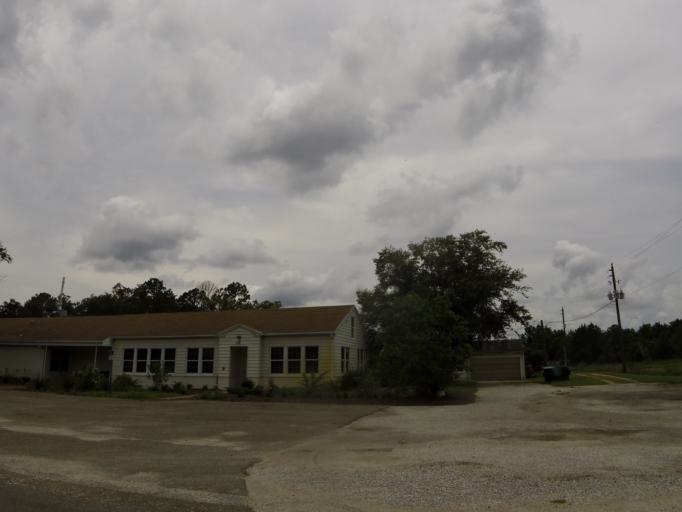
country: US
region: Florida
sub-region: Putnam County
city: East Palatka
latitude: 29.7216
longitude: -81.4941
